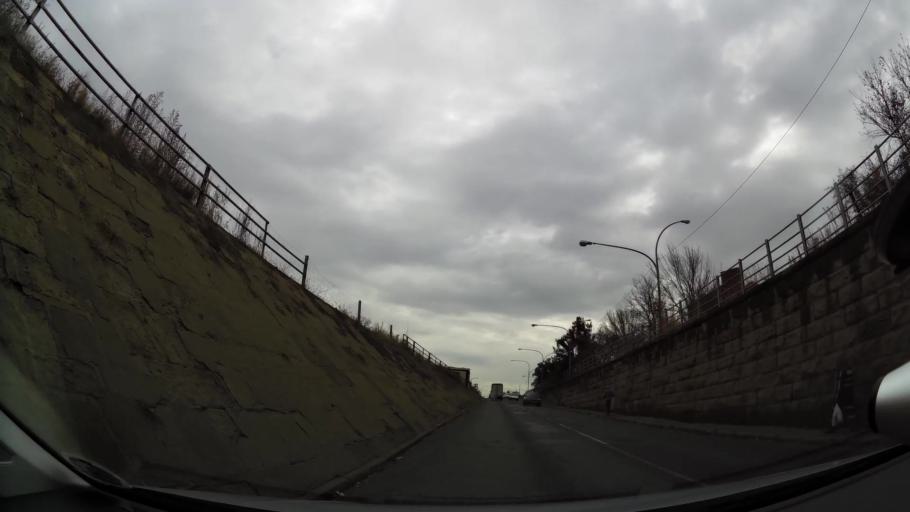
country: ZA
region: Orange Free State
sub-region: Fezile Dabi District Municipality
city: Kroonstad
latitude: -27.6598
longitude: 27.2314
